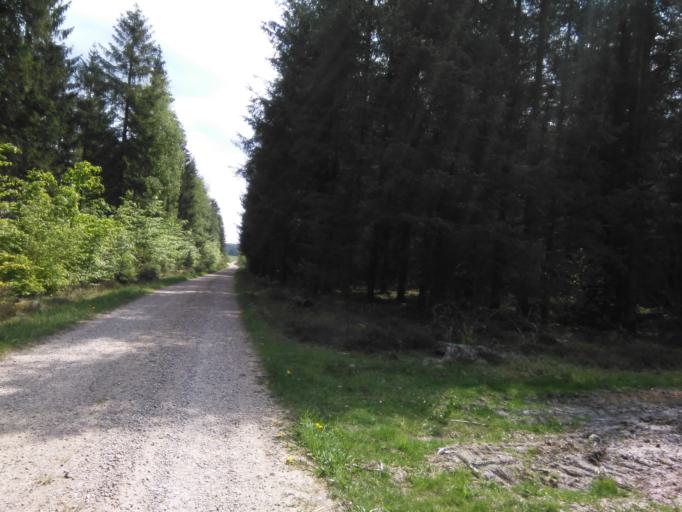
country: DK
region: Central Jutland
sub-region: Silkeborg Kommune
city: Svejbaek
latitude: 56.0564
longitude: 9.6591
